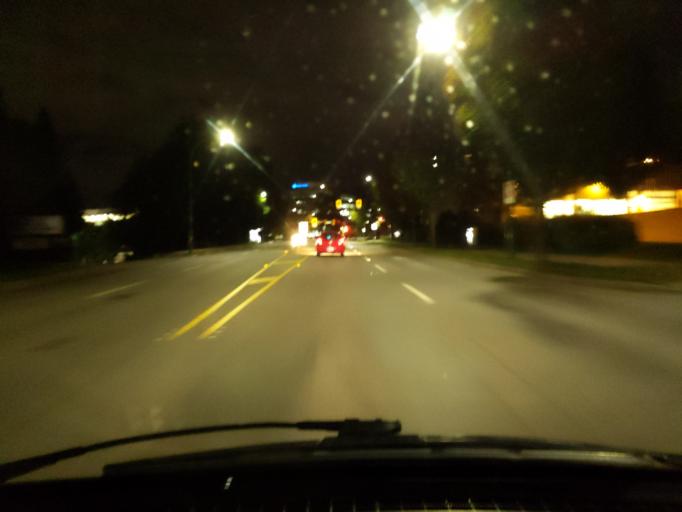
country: CA
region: British Columbia
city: Burnaby
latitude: 49.2564
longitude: -123.0119
